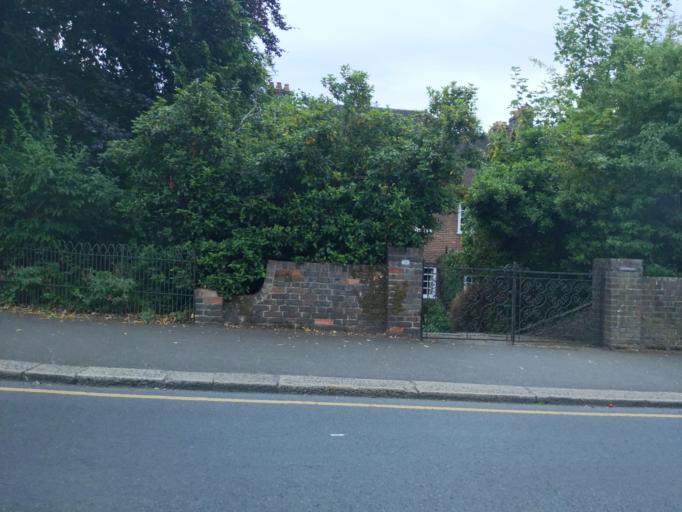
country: GB
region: England
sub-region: Greater London
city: South Croydon
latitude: 51.3606
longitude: -0.0852
